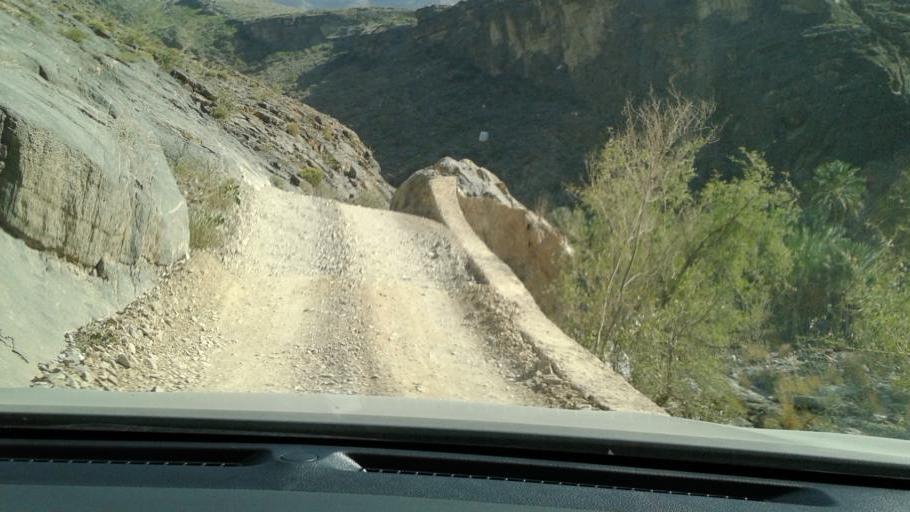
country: OM
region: Al Batinah
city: Bayt al `Awabi
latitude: 23.1960
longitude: 57.3906
